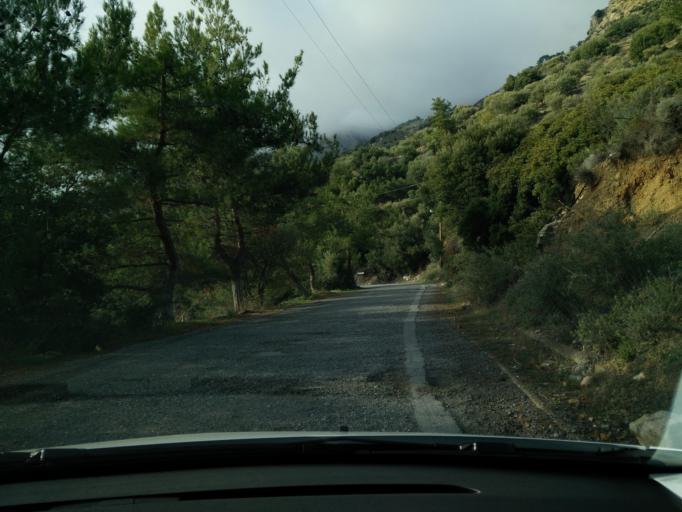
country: GR
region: Crete
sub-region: Nomos Lasithiou
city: Gra Liyia
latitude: 35.0291
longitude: 25.5519
